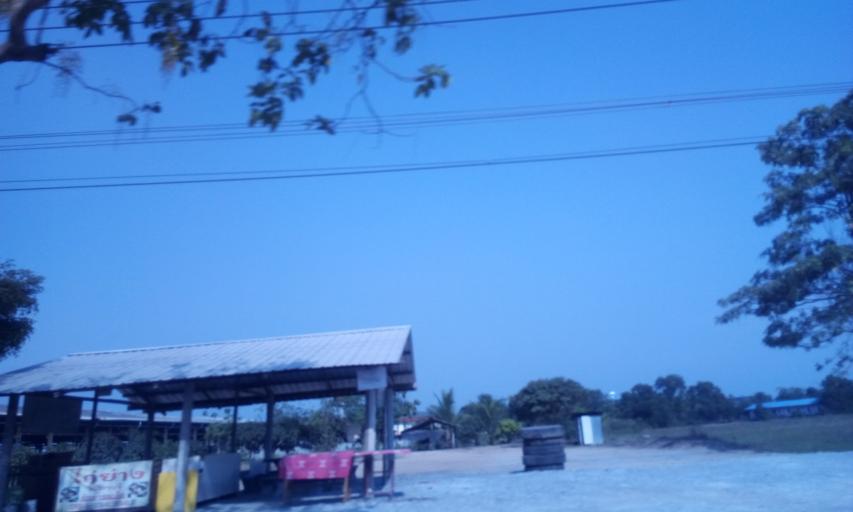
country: TH
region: Nonthaburi
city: Sai Noi
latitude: 14.0336
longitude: 100.3123
